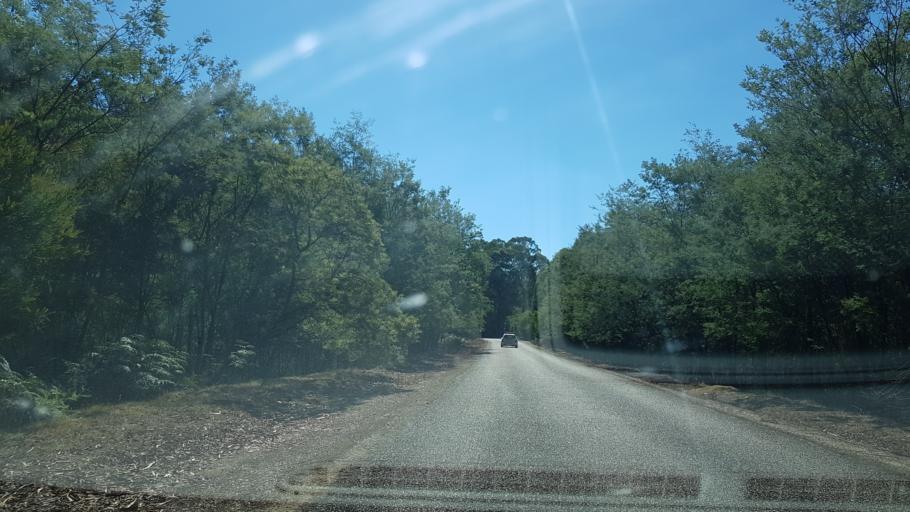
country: AU
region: Victoria
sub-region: Mansfield
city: Mansfield
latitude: -36.8959
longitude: 146.3862
